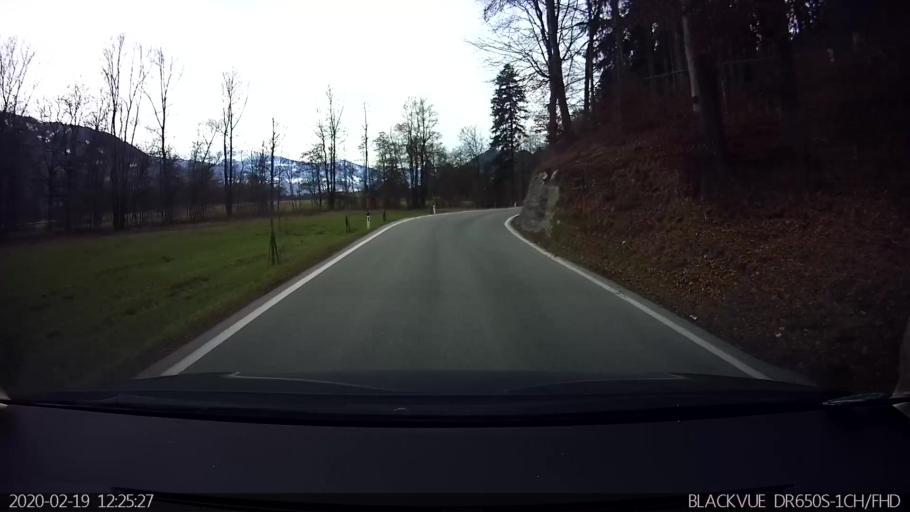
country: AT
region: Tyrol
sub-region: Politischer Bezirk Schwaz
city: Buch bei Jenbach
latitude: 47.3803
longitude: 11.7350
